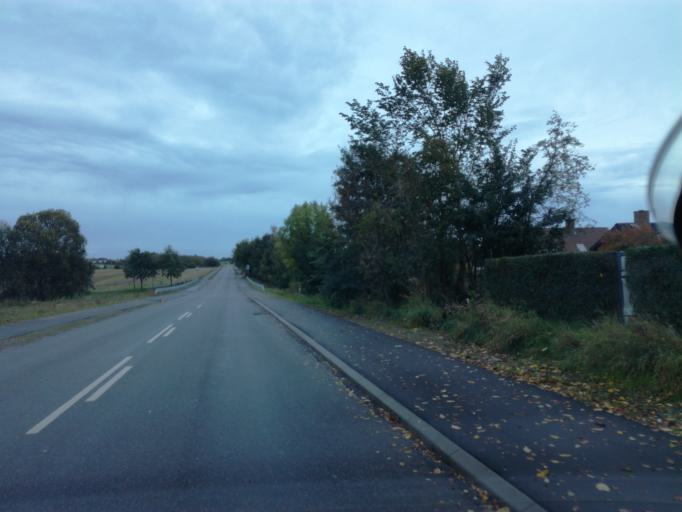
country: DK
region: South Denmark
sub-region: Fredericia Kommune
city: Fredericia
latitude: 55.6133
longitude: 9.7476
